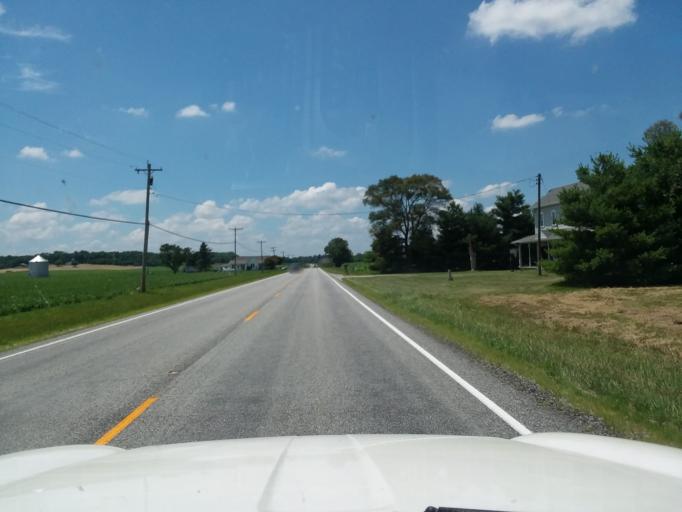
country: US
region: Indiana
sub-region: Johnson County
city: Princes Lakes
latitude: 39.4103
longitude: -86.0734
